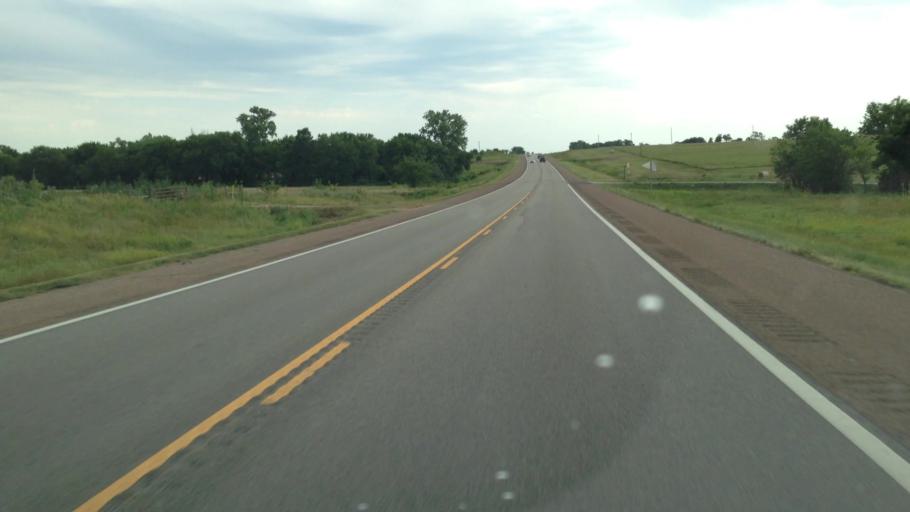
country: US
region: Kansas
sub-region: Woodson County
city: Yates Center
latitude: 38.0139
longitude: -95.7392
